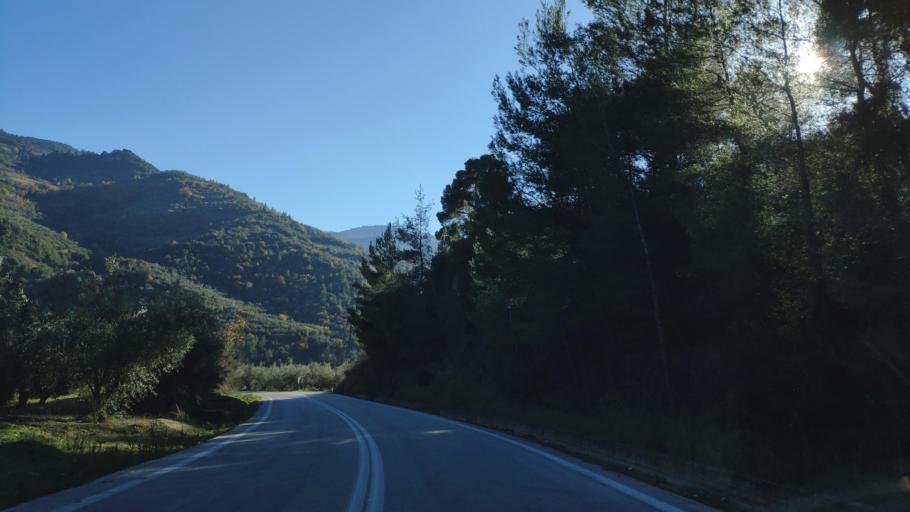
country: GR
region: Peloponnese
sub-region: Nomos Korinthias
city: Xylokastro
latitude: 38.0021
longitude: 22.5040
